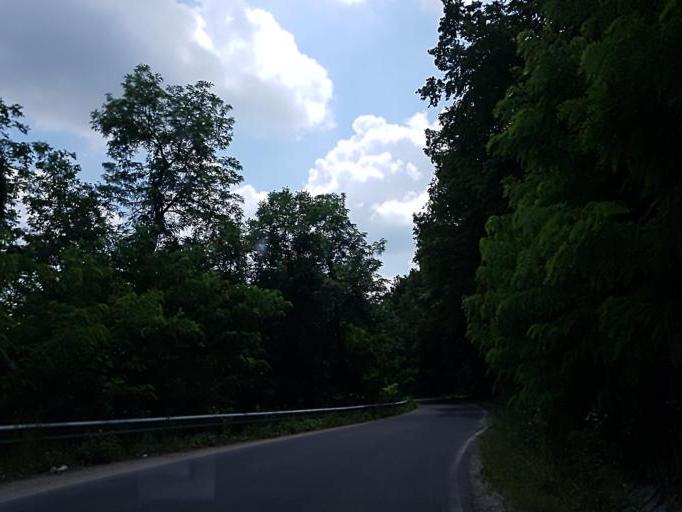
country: RO
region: Sibiu
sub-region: Comuna Seica Mare
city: Seica Mare
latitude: 46.0382
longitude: 24.1601
